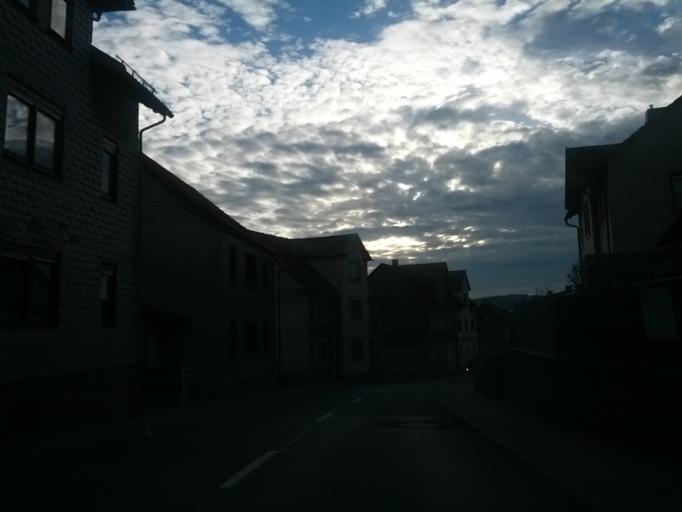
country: DE
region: Thuringia
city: Brotterode
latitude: 50.8260
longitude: 10.4487
